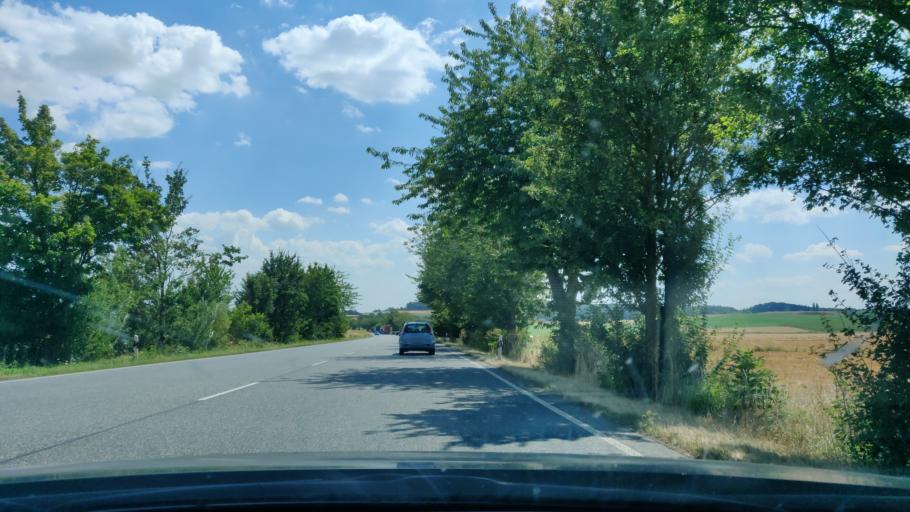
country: DE
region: Hesse
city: Fritzlar
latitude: 51.1121
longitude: 9.2618
